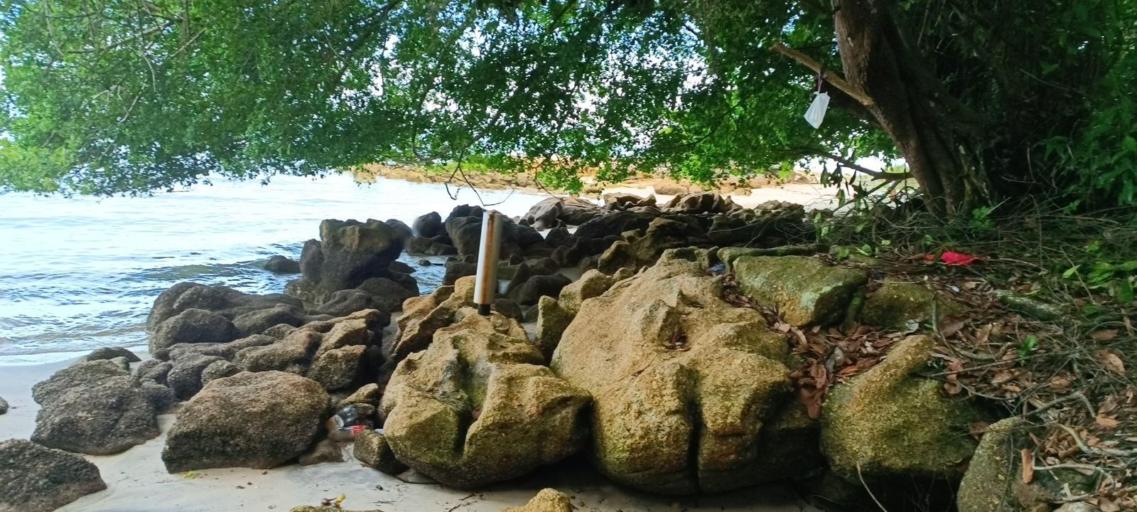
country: MY
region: Penang
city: Kampung Sungai Ara
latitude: 5.2822
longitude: 100.2119
